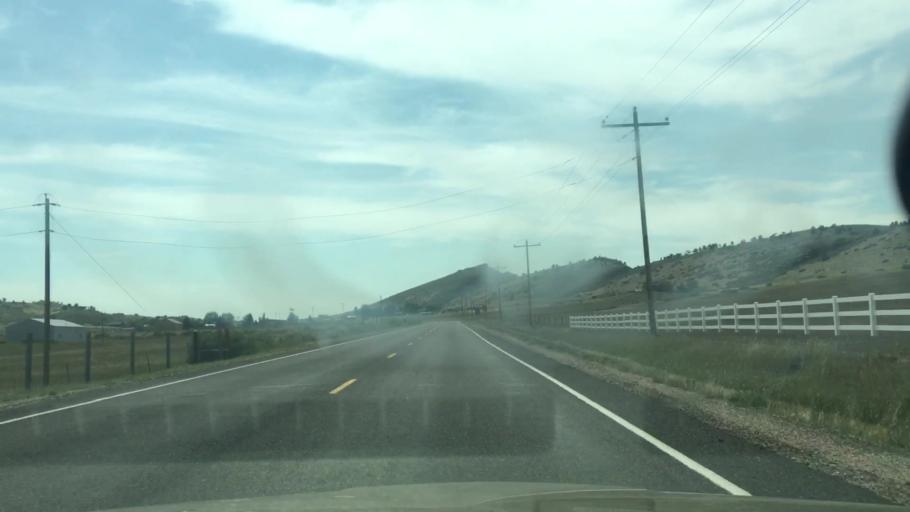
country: US
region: Colorado
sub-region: Larimer County
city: Campion
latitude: 40.3754
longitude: -105.1921
